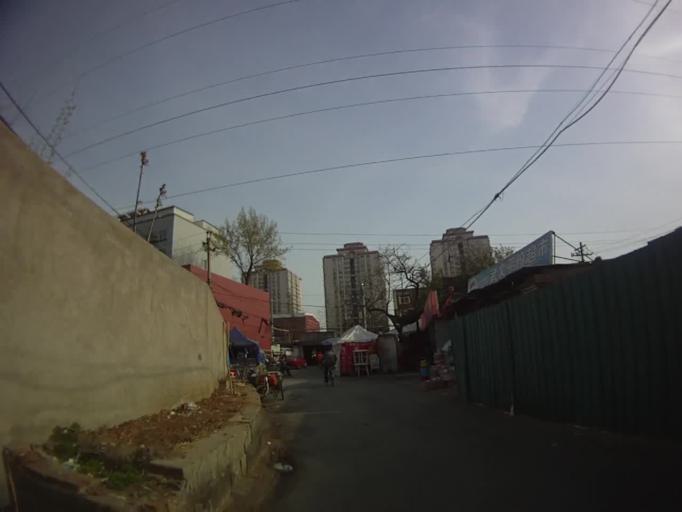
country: CN
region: Beijing
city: Chaowai
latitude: 39.9014
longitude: 116.4425
